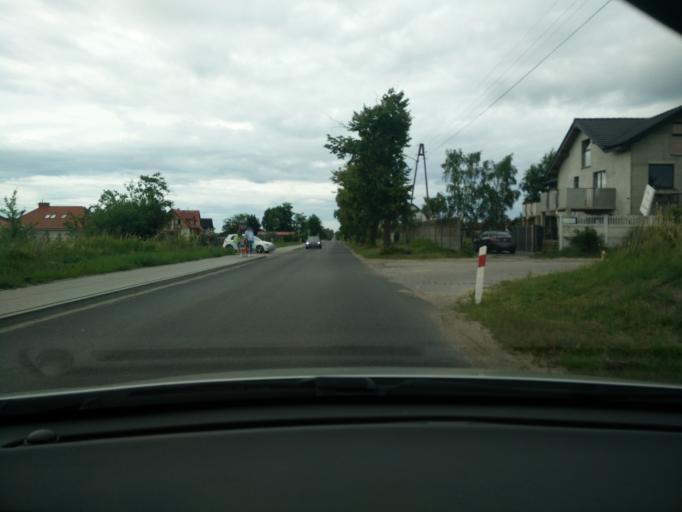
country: PL
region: Pomeranian Voivodeship
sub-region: Powiat pucki
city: Mosty
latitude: 54.6185
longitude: 18.4963
